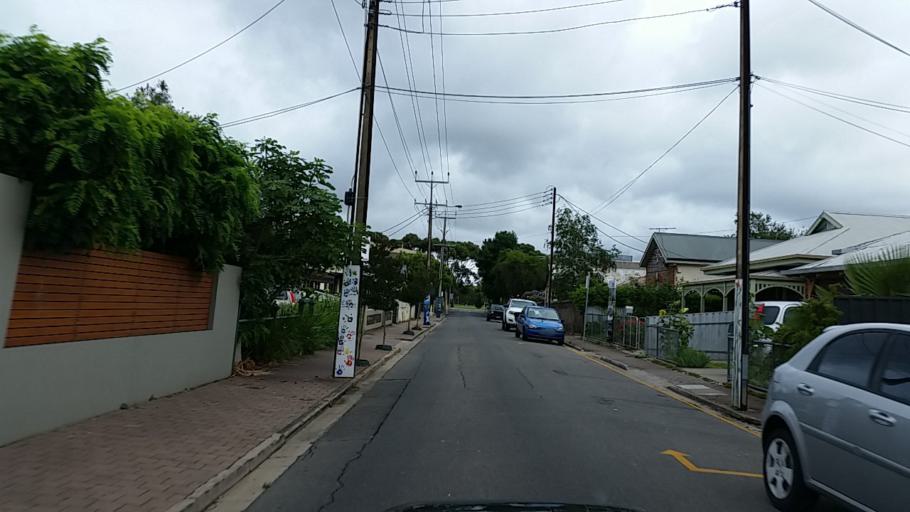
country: AU
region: South Australia
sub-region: Unley
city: Unley
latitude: -34.9425
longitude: 138.6080
